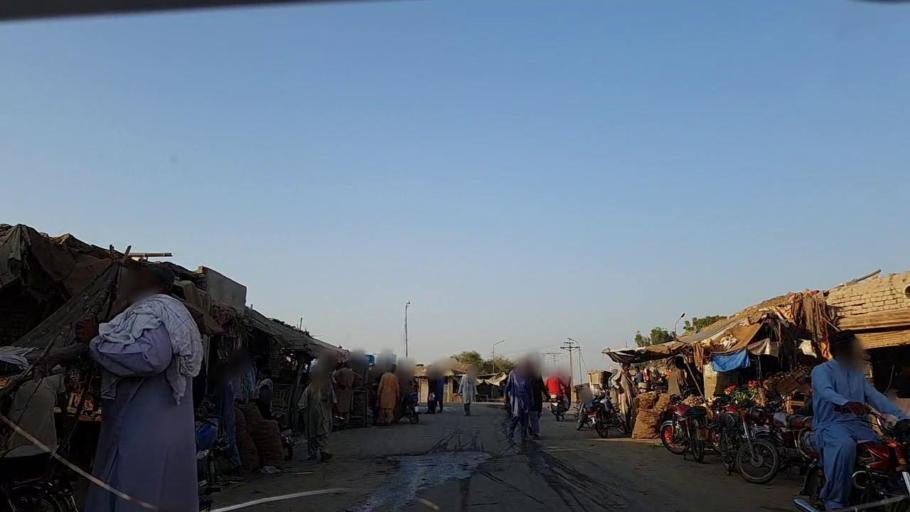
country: PK
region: Sindh
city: Rustam jo Goth
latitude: 28.0215
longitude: 68.8124
